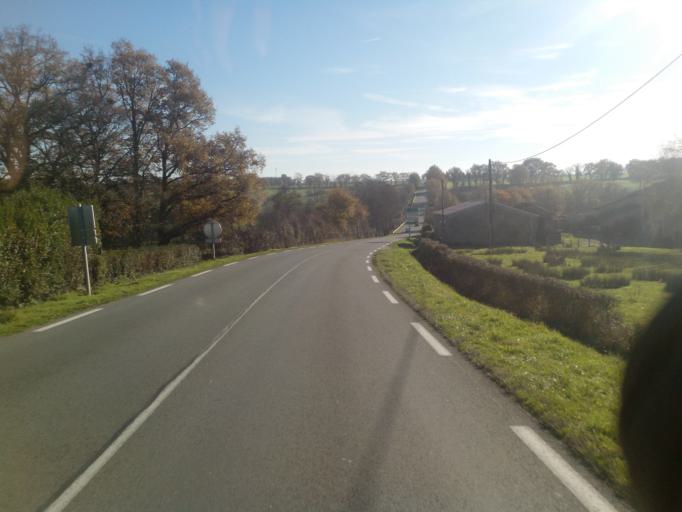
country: FR
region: Poitou-Charentes
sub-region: Departement de la Vienne
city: Saulge
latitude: 46.3277
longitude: 0.8153
